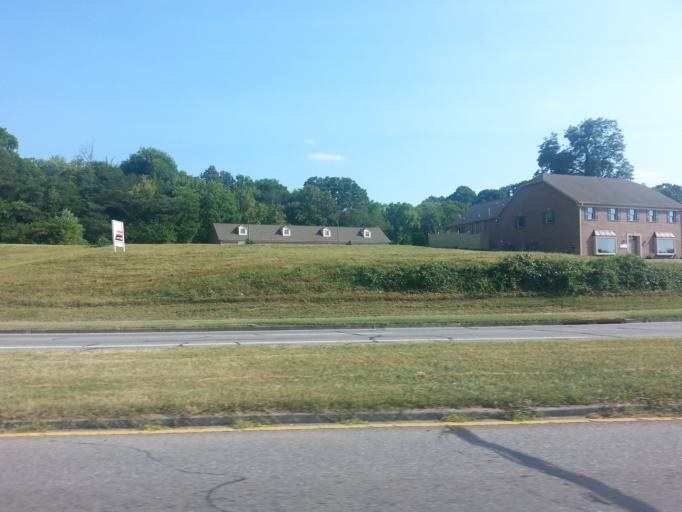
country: US
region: Tennessee
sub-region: Blount County
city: Maryville
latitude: 35.7518
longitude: -83.9848
